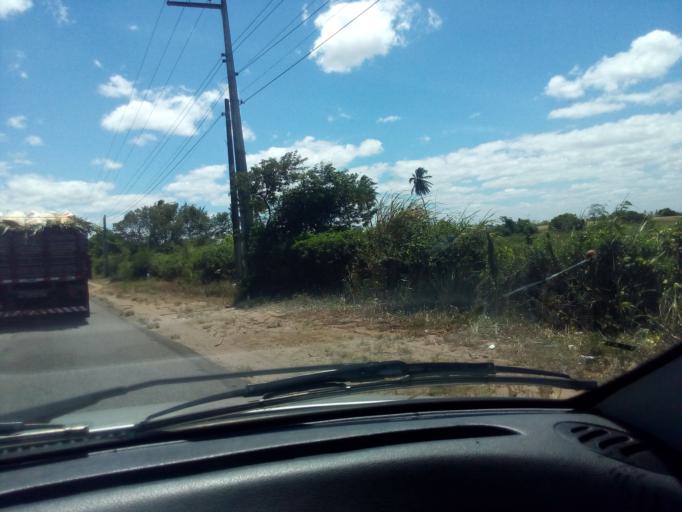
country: BR
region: Rio Grande do Norte
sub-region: Sao Goncalo Do Amarante
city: Sao Goncalo do Amarante
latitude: -5.7959
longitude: -35.3289
